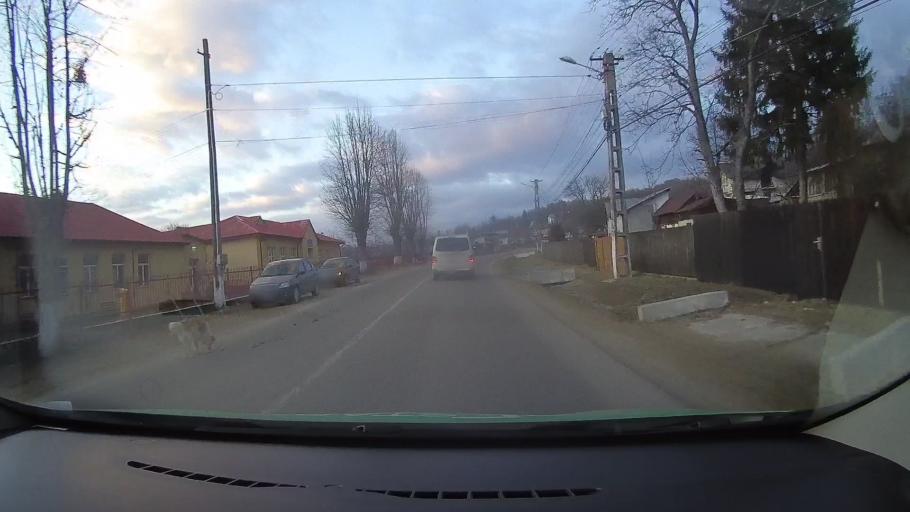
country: RO
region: Dambovita
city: Iedera de Jos
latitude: 45.0252
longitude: 25.6354
